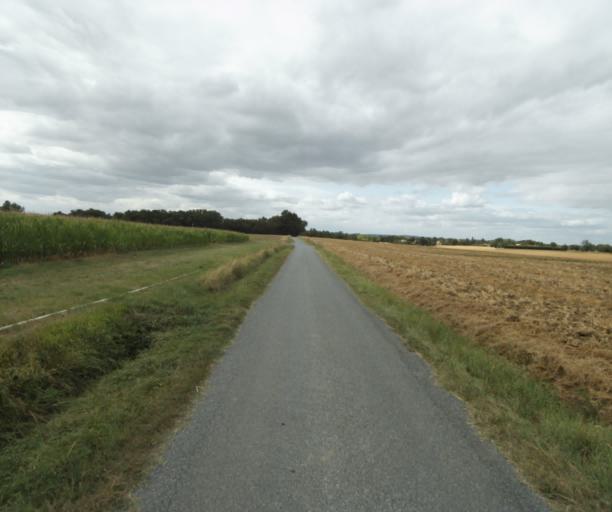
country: FR
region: Midi-Pyrenees
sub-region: Departement du Tarn
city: Soreze
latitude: 43.4834
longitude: 2.0595
